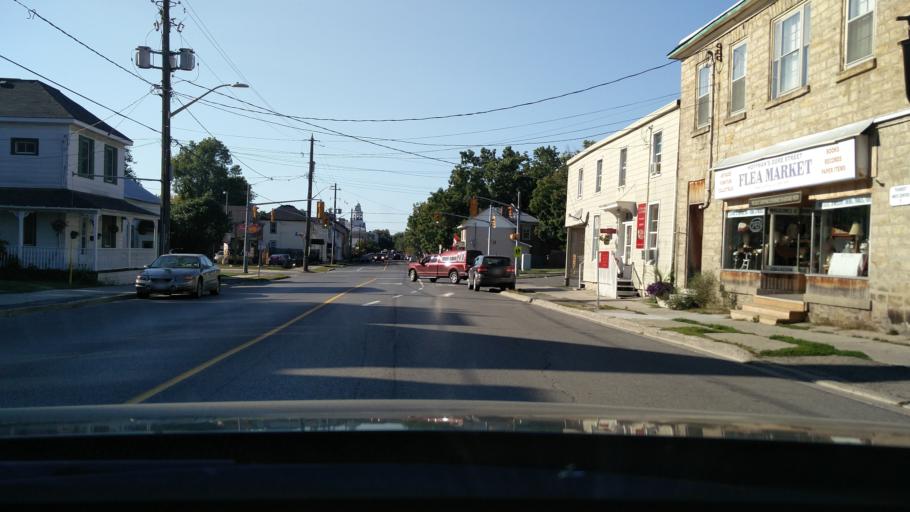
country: CA
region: Ontario
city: Perth
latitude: 44.8966
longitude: -76.2455
